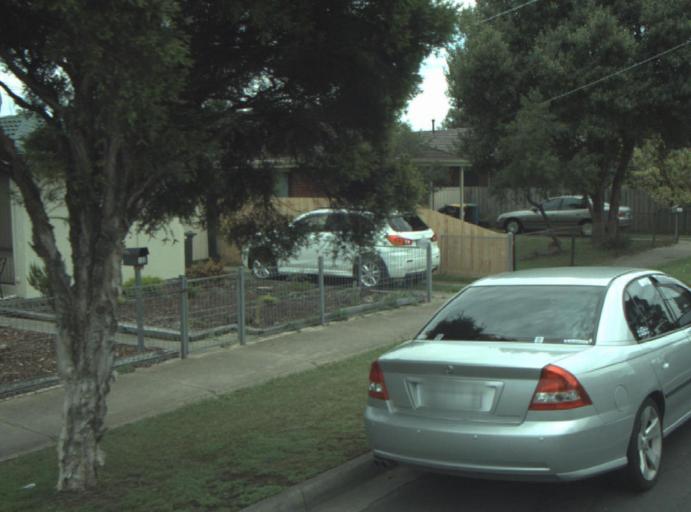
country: AU
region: Victoria
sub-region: Greater Geelong
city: Breakwater
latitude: -38.1800
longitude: 144.4013
